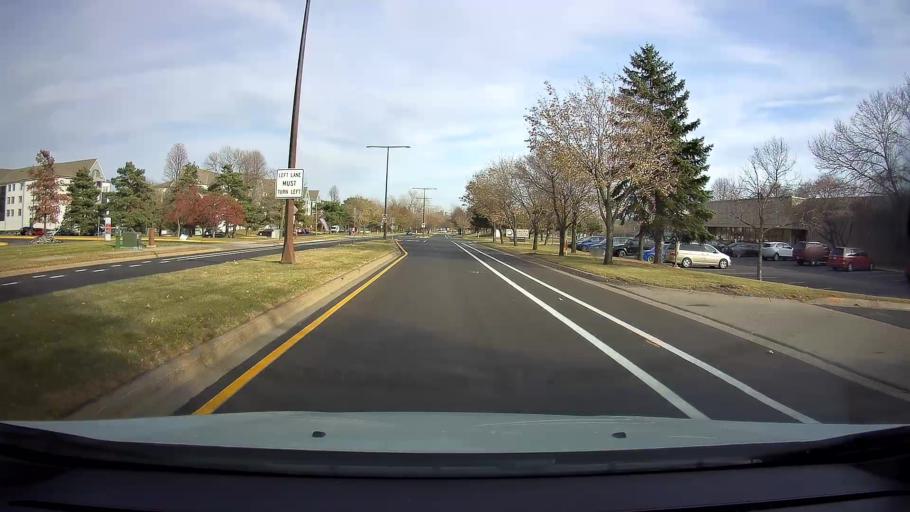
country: US
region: Minnesota
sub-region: Ramsey County
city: Falcon Heights
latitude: 44.9707
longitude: -93.1523
